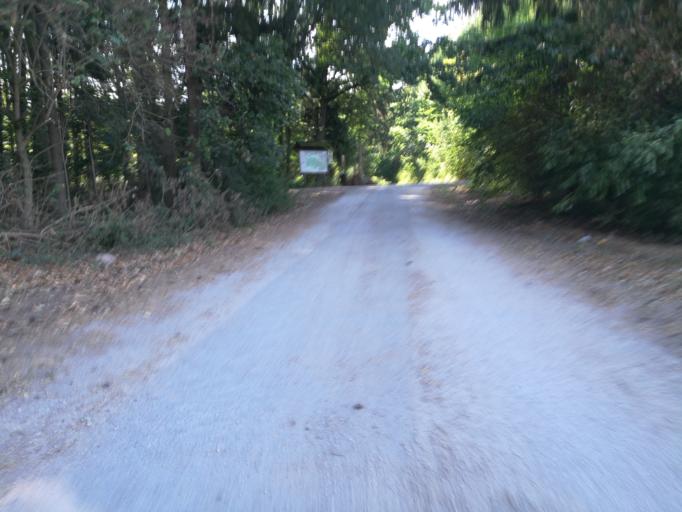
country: DE
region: Bavaria
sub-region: Regierungsbezirk Mittelfranken
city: Seukendorf
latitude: 49.4765
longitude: 10.9240
